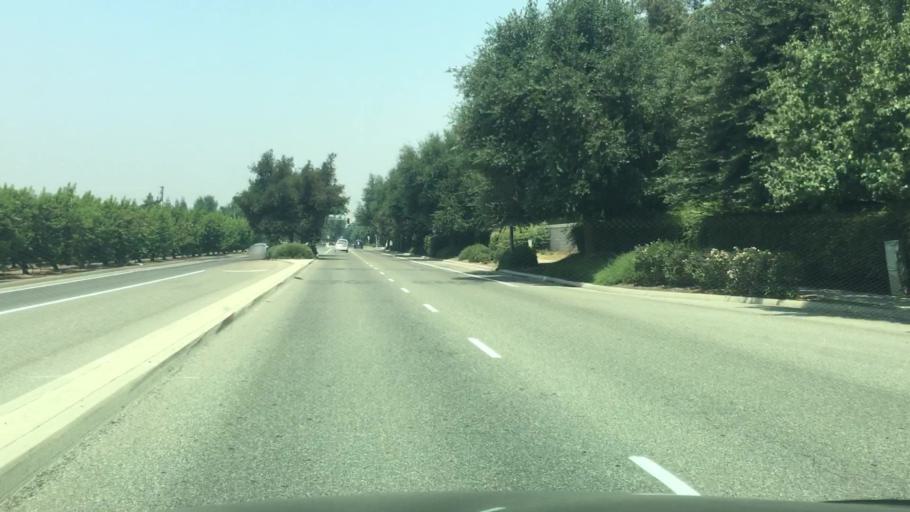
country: US
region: California
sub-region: Fresno County
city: Clovis
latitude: 36.8430
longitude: -119.7111
